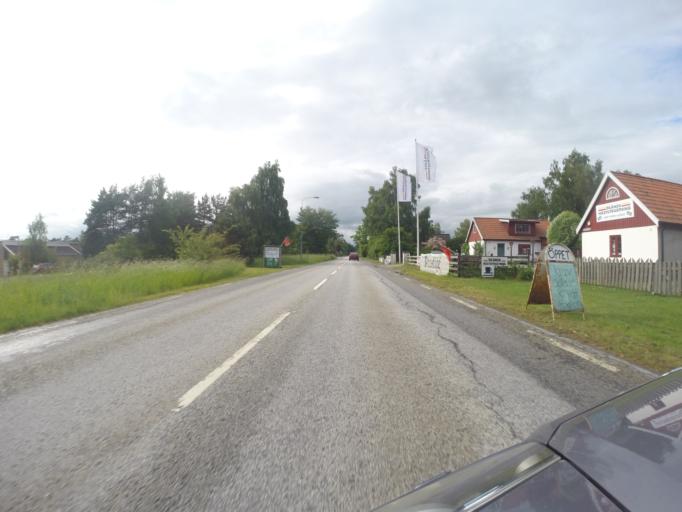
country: SE
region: Skane
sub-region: Kavlinge Kommun
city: Hofterup
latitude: 55.8086
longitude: 12.9809
